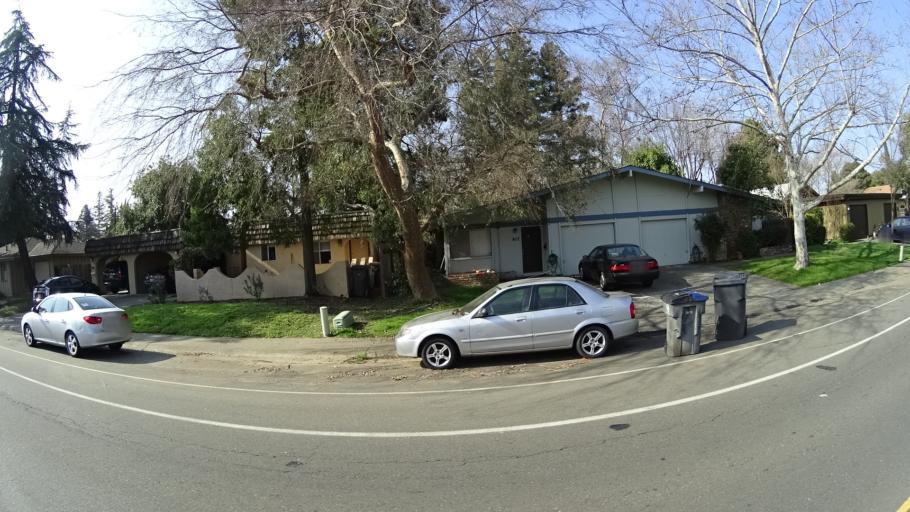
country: US
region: California
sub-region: Yolo County
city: Davis
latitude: 38.5510
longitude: -121.7703
